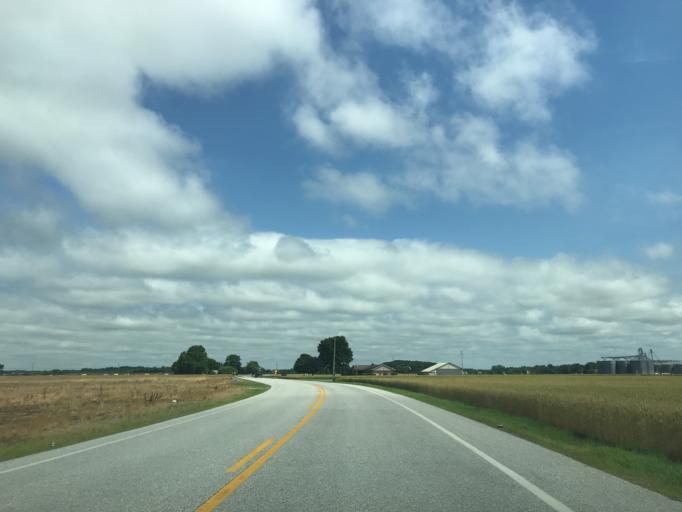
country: US
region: Maryland
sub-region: Caroline County
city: Ridgely
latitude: 38.9300
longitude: -75.8933
